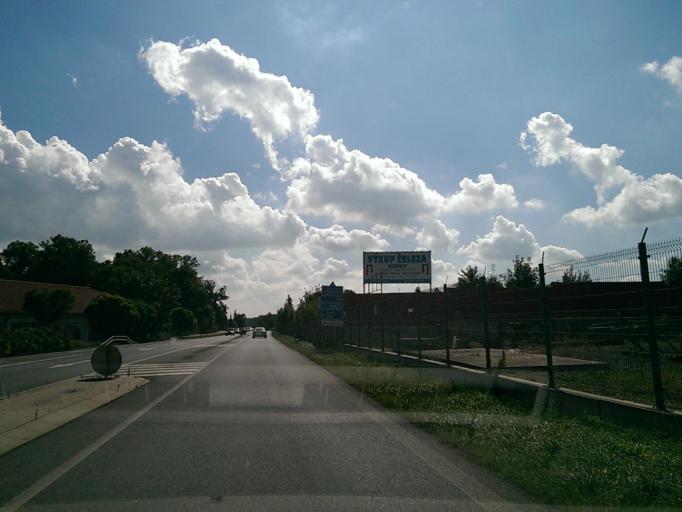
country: CZ
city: Doksy
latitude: 50.5653
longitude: 14.6487
